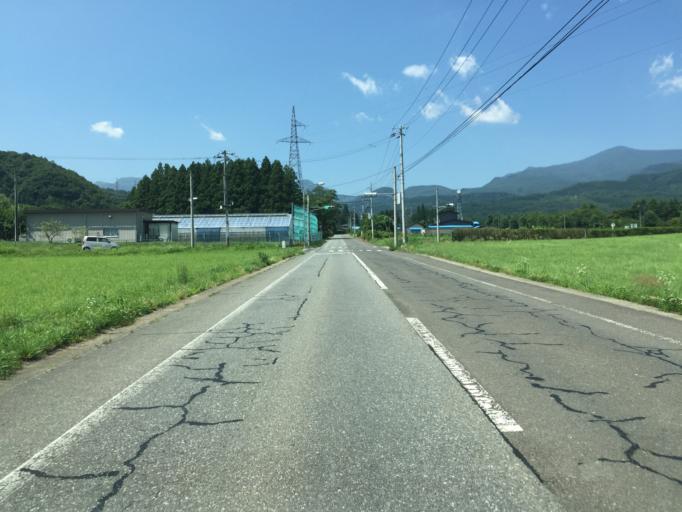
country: JP
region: Fukushima
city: Fukushima-shi
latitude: 37.7064
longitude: 140.3658
